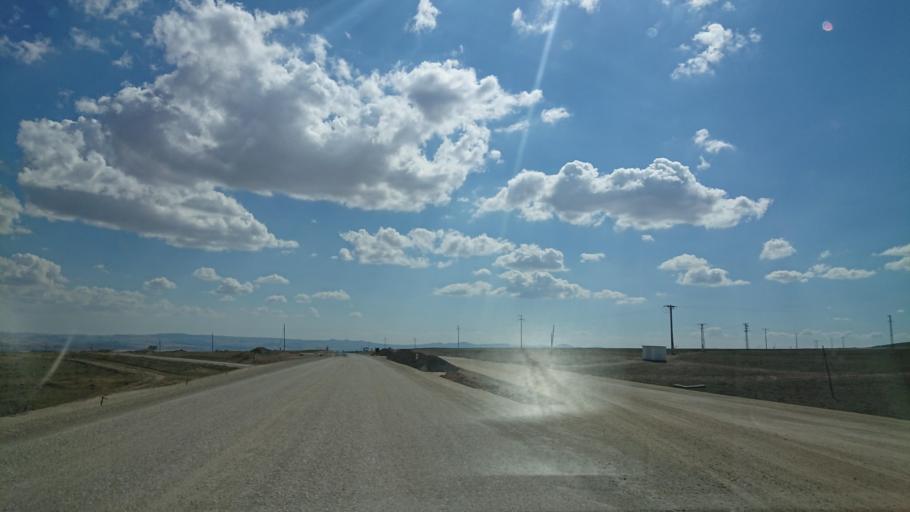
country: TR
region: Kirsehir
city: Kirsehir
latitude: 39.1330
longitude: 34.0446
